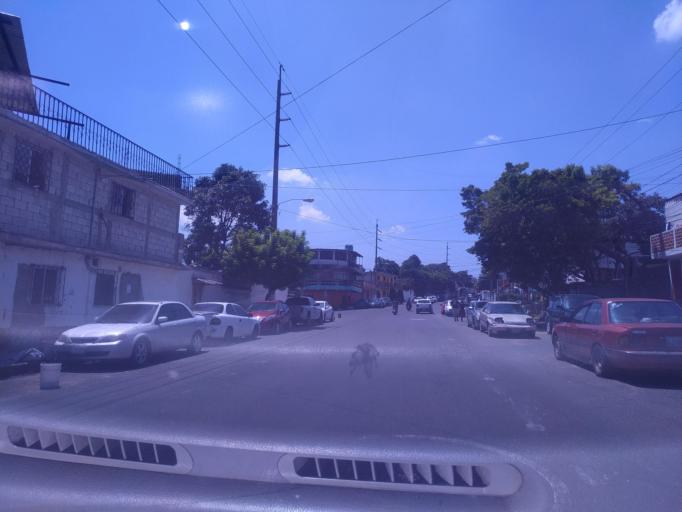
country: GT
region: Guatemala
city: Mixco
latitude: 14.6819
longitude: -90.5696
